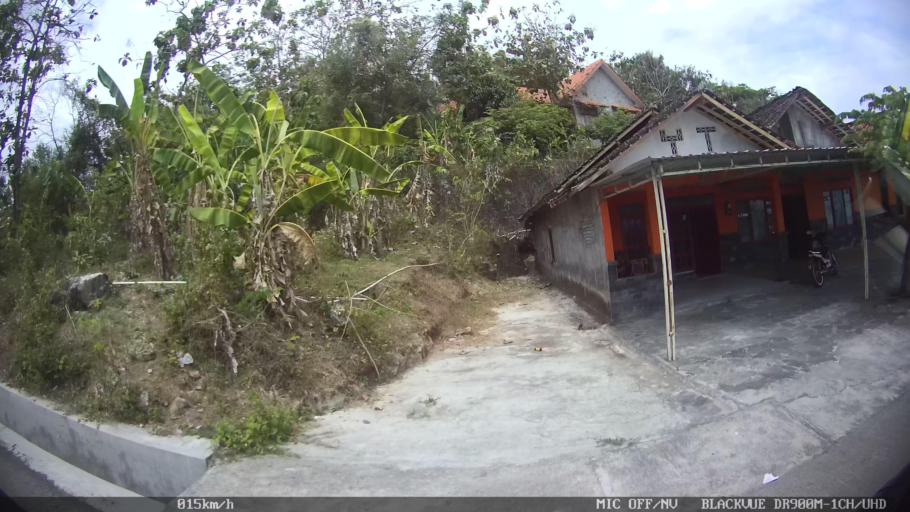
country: ID
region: Central Java
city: Candi Prambanan
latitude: -7.7835
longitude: 110.5029
